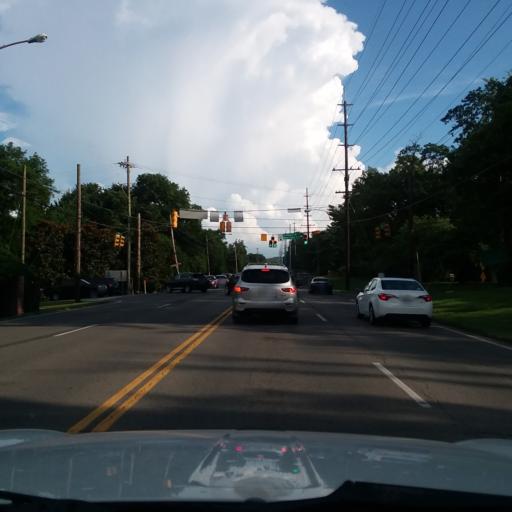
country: US
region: Tennessee
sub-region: Davidson County
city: Oak Hill
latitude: 36.0668
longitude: -86.7743
